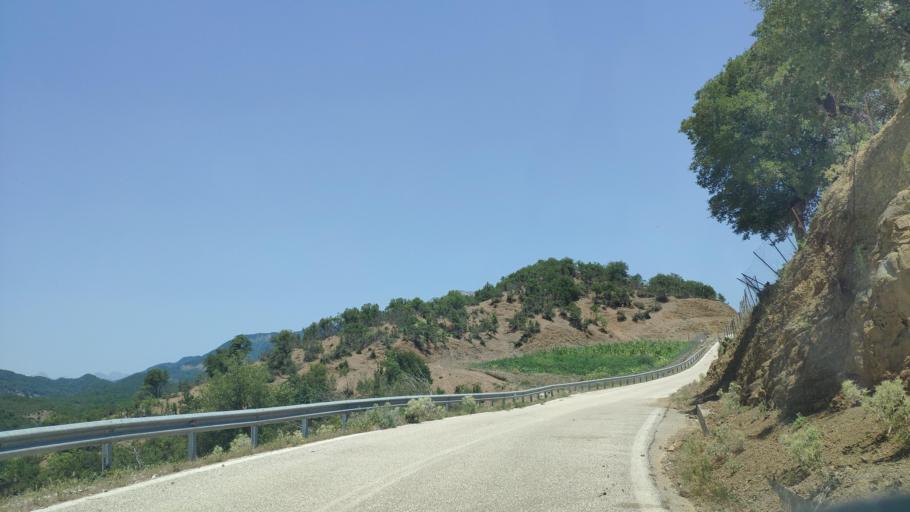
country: GR
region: Epirus
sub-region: Nomos Artas
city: Ano Kalentini
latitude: 39.2209
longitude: 21.3488
